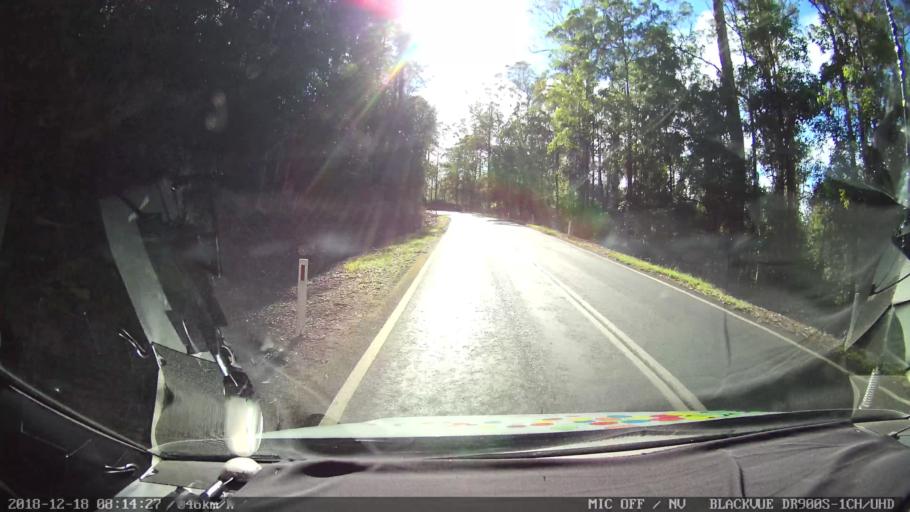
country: AU
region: New South Wales
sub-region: Kyogle
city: Kyogle
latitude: -28.3361
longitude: 152.6814
